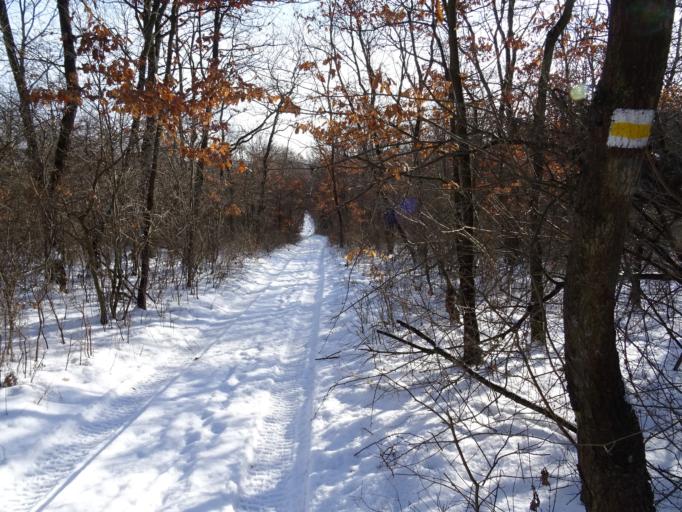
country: HU
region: Komarom-Esztergom
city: Oroszlany
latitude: 47.4852
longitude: 18.3578
